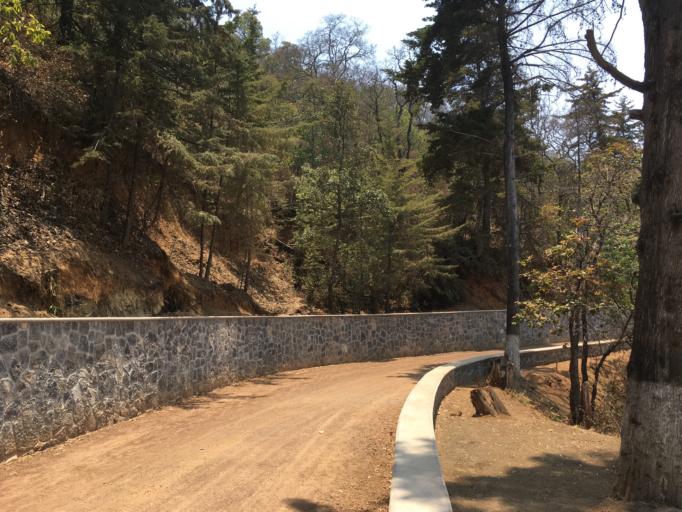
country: MX
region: Michoacan
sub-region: Patzcuaro
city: Santa Ana Chapitiro
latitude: 19.5150
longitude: -101.6386
